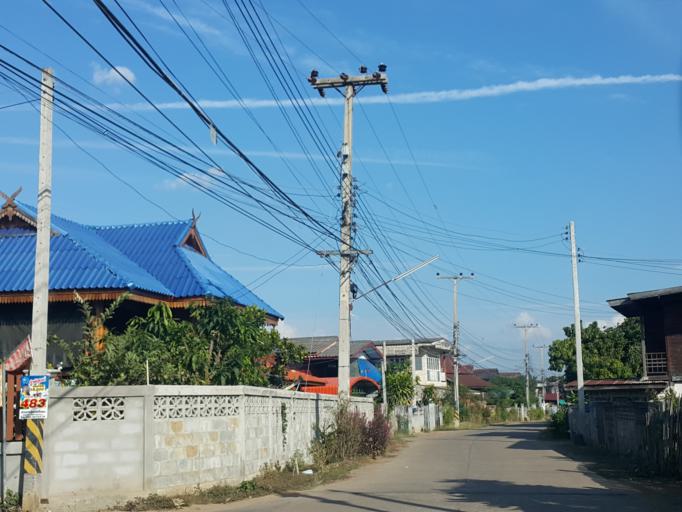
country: TH
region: Sukhothai
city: Thung Saliam
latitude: 17.3129
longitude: 99.5536
